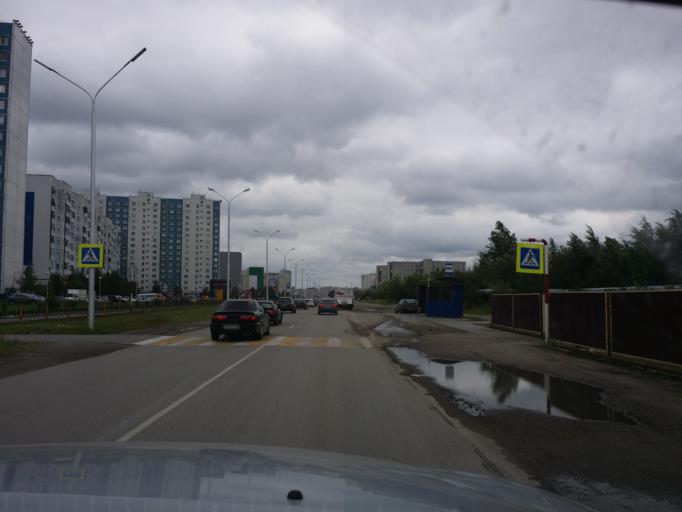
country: RU
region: Khanty-Mansiyskiy Avtonomnyy Okrug
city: Nizhnevartovsk
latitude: 60.9524
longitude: 76.5817
